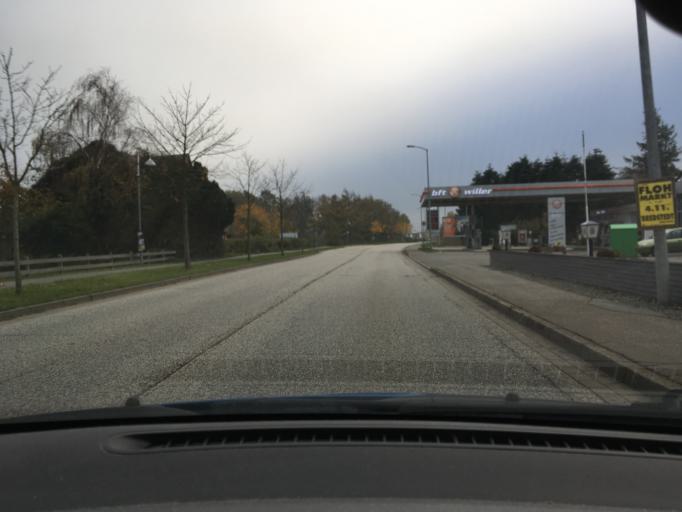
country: DE
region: Schleswig-Holstein
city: Bargum
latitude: 54.6859
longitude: 8.9575
